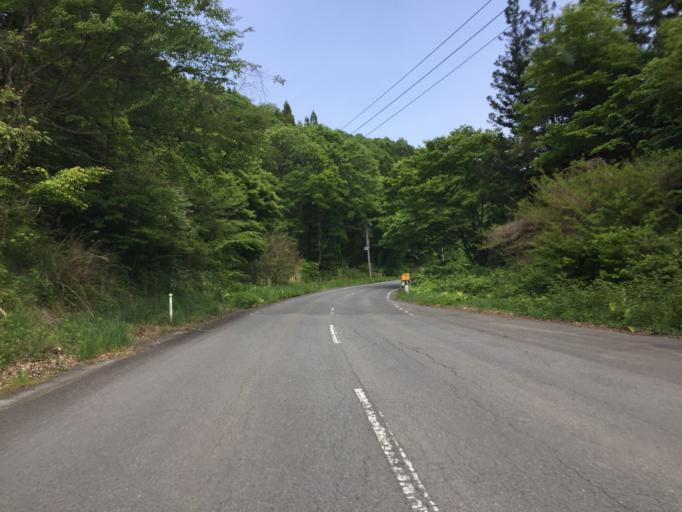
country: JP
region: Ibaraki
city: Kitaibaraki
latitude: 36.9811
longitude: 140.6234
